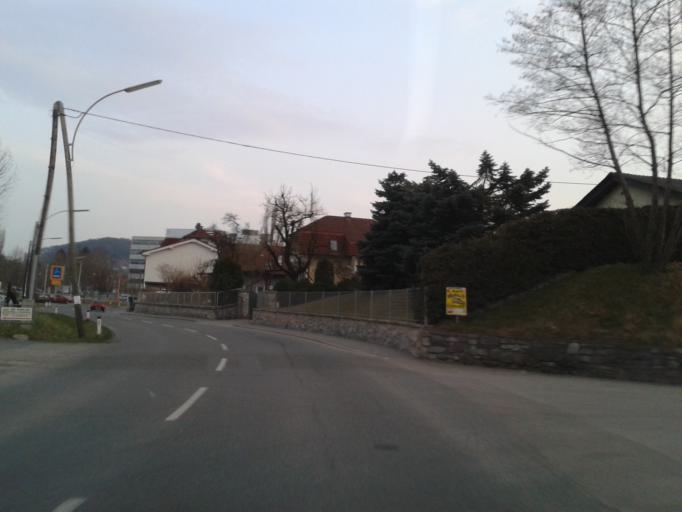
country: AT
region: Styria
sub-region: Politischer Bezirk Graz-Umgebung
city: Stattegg
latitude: 47.1111
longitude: 15.4223
